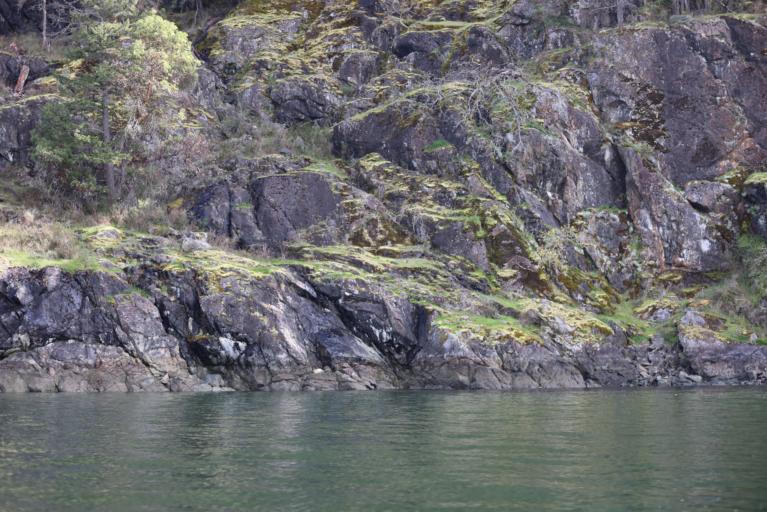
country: CA
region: British Columbia
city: Langford
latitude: 48.5308
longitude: -123.5374
